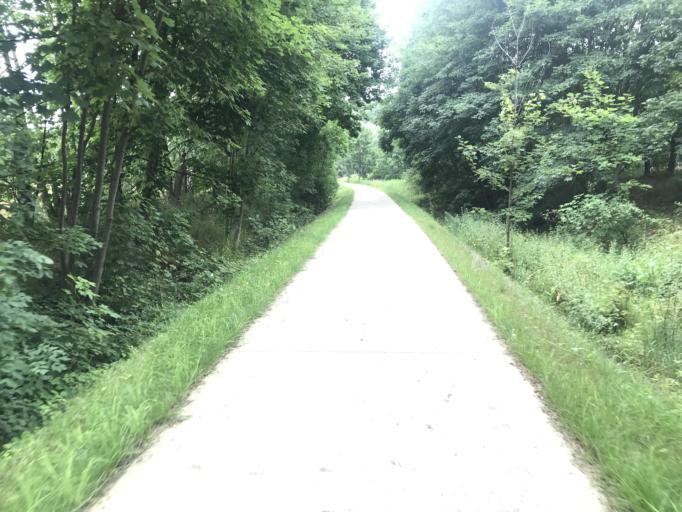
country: DE
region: Saxony-Anhalt
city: Rieder
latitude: 51.7271
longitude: 11.1891
